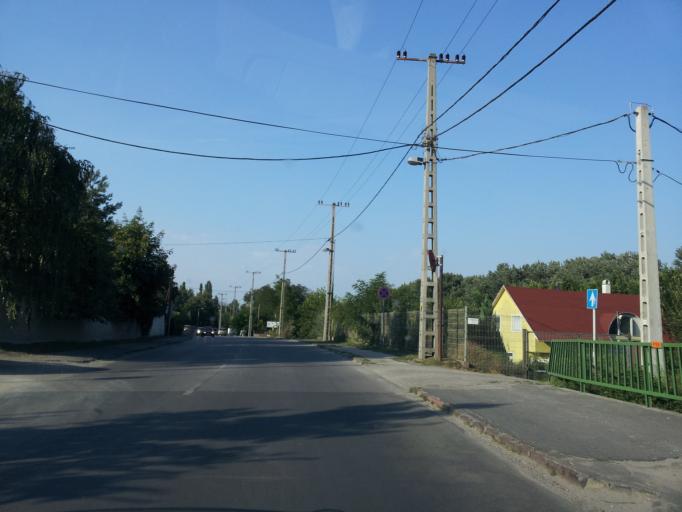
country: HU
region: Pest
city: Szentendre
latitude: 47.6881
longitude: 19.0853
